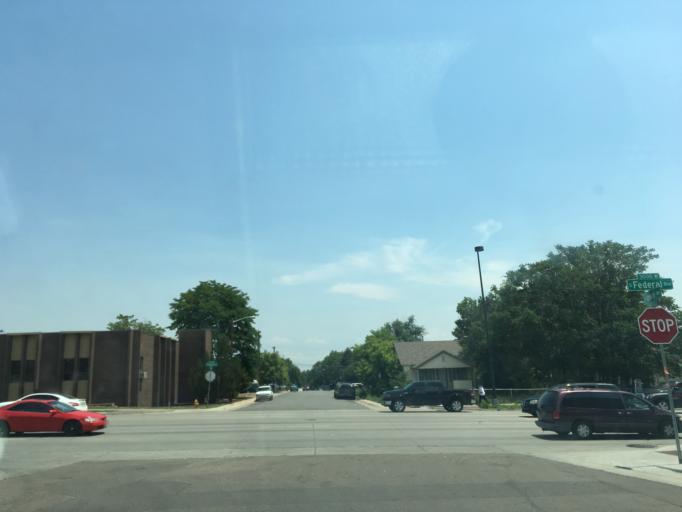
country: US
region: Colorado
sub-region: Arapahoe County
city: Sheridan
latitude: 39.6877
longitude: -105.0255
